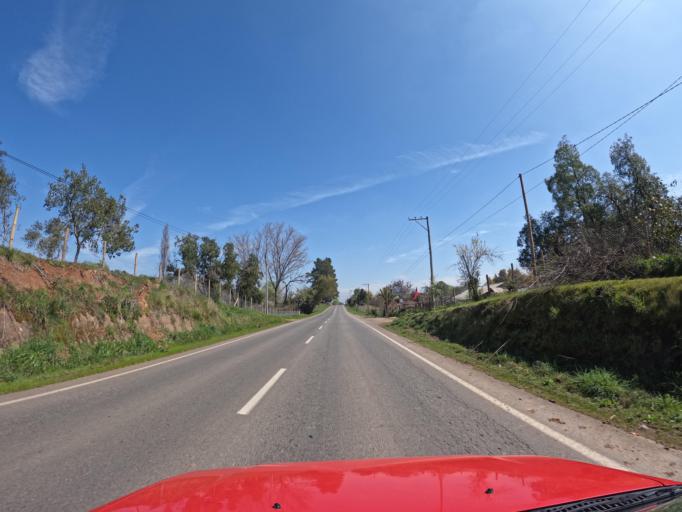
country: CL
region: Maule
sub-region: Provincia de Talca
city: San Clemente
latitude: -35.4851
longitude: -71.2772
